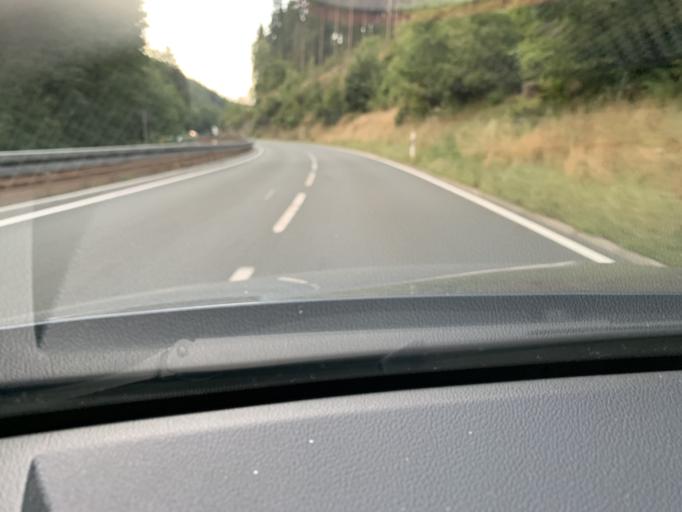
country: DE
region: Thuringia
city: Steinach
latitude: 50.4139
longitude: 11.1761
